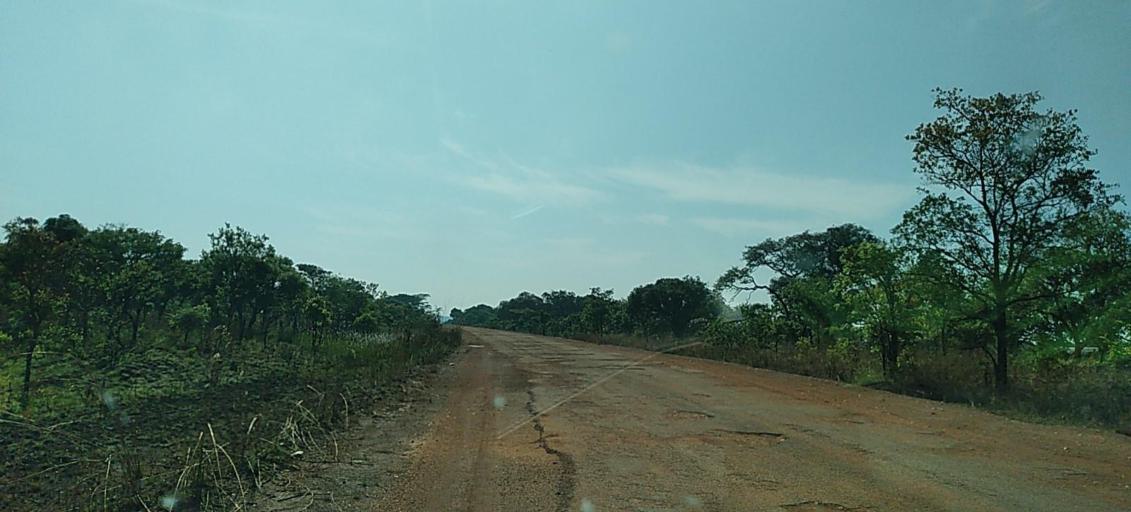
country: ZM
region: North-Western
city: Mwinilunga
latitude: -11.8216
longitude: 25.0987
